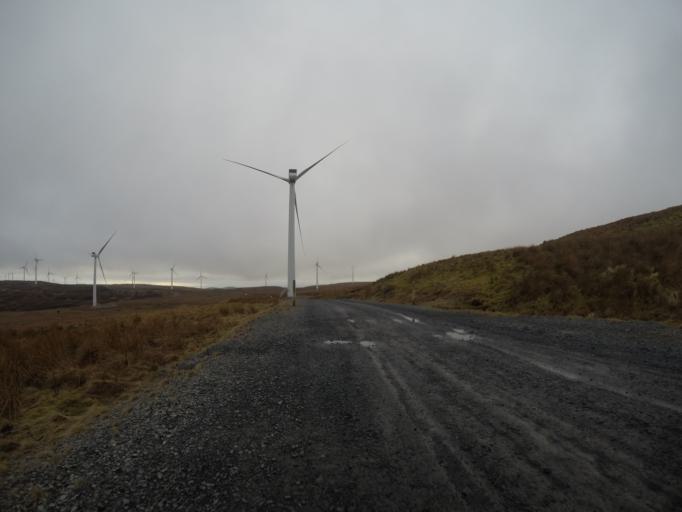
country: GB
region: Scotland
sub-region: North Ayrshire
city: Fairlie
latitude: 55.7588
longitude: -4.7942
